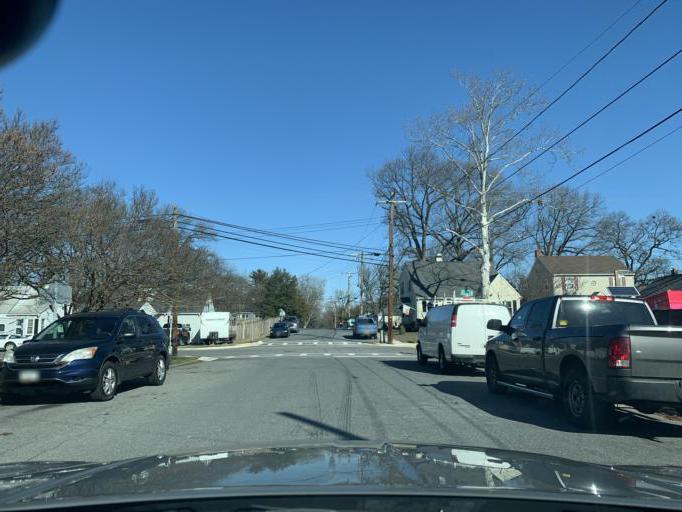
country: US
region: Maryland
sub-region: Anne Arundel County
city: Glen Burnie
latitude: 39.1607
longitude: -76.6311
